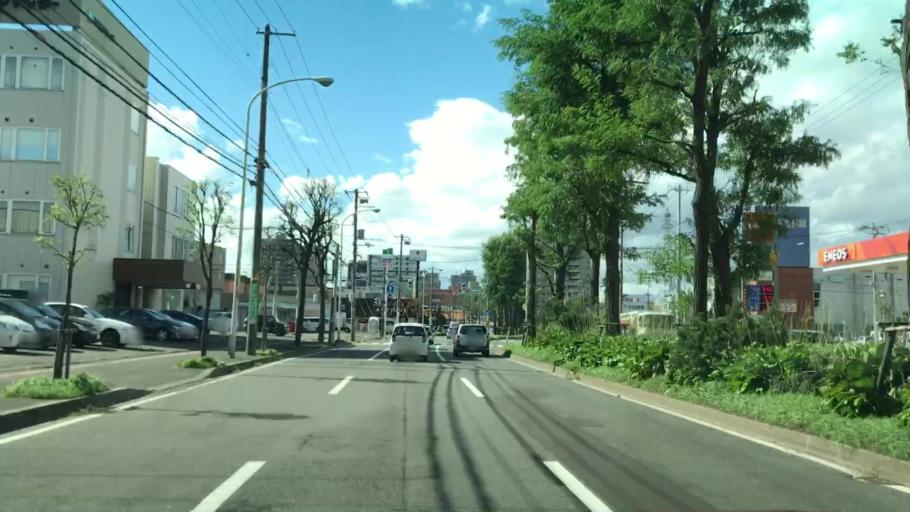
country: JP
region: Hokkaido
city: Sapporo
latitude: 43.0330
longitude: 141.4286
